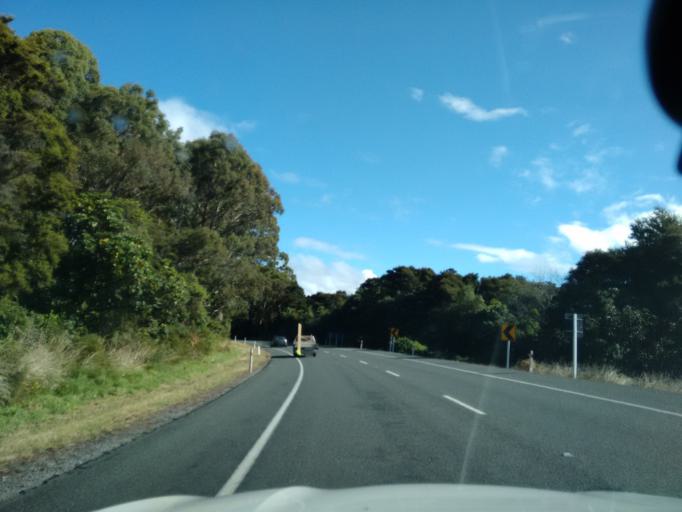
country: NZ
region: Waikato
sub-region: Taupo District
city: Taupo
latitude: -38.8571
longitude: 176.0121
